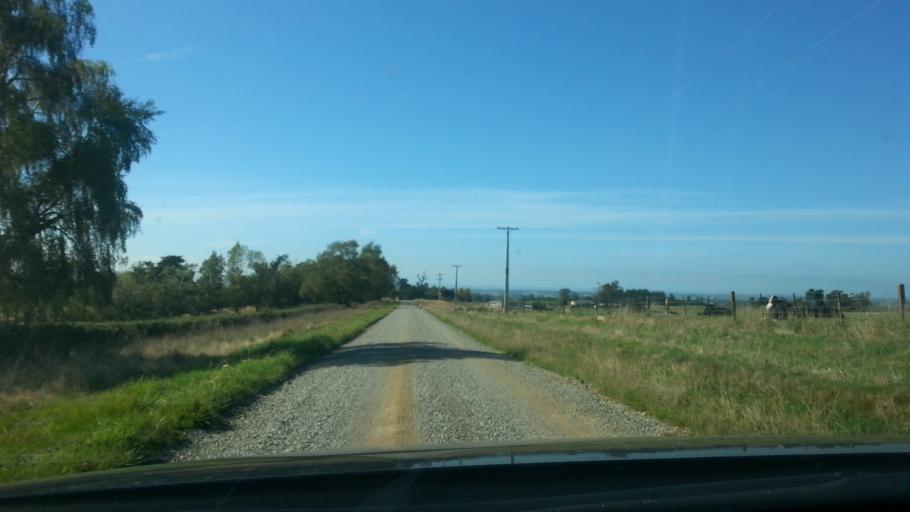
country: NZ
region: Otago
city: Oamaru
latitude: -44.7078
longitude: 170.9939
